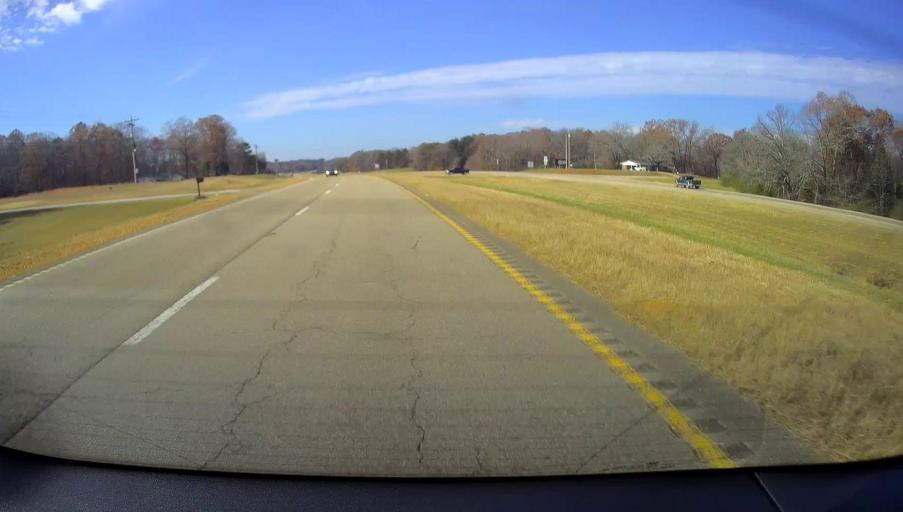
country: US
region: Mississippi
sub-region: Tippah County
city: Ripley
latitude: 34.9487
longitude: -88.8106
